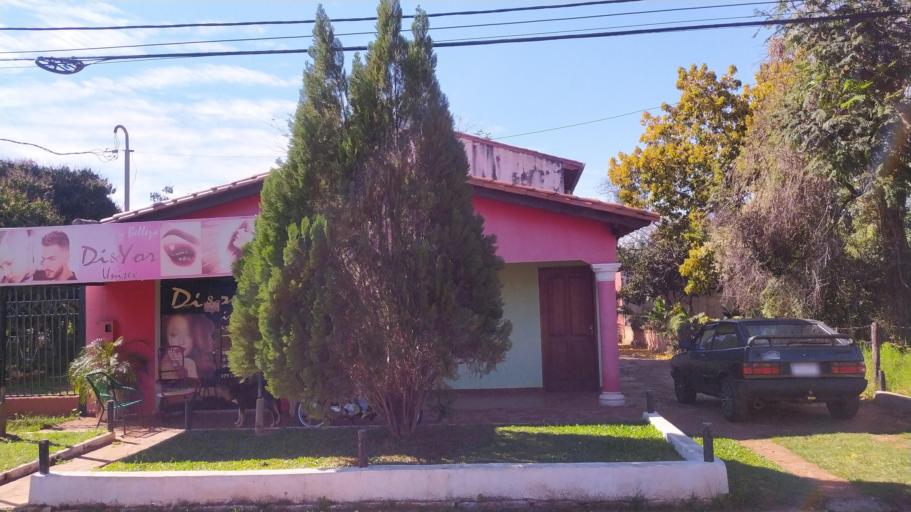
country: PY
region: Misiones
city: San Juan Bautista
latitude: -26.6722
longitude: -57.1376
